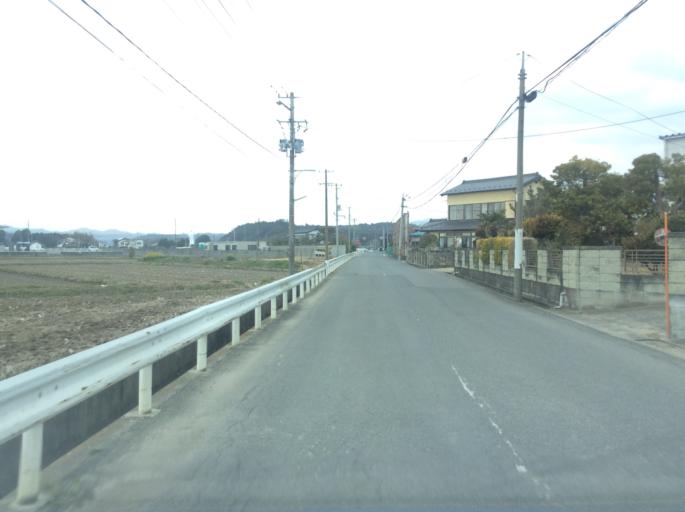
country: JP
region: Fukushima
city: Iwaki
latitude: 37.0823
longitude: 140.9670
